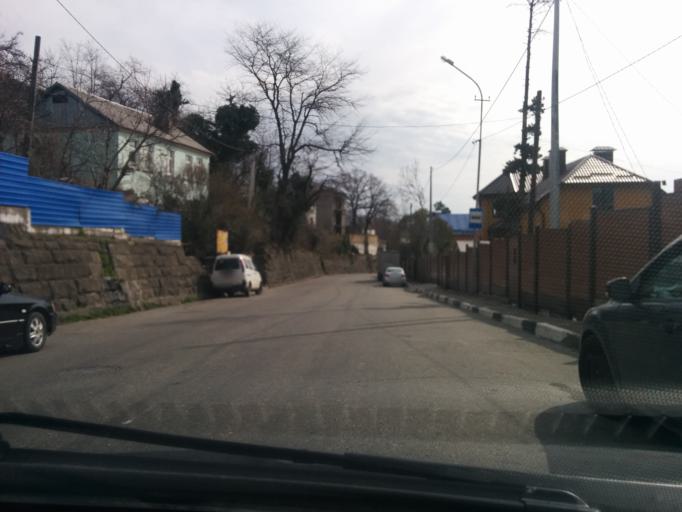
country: RU
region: Krasnodarskiy
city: Tuapse
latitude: 44.1039
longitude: 39.0681
